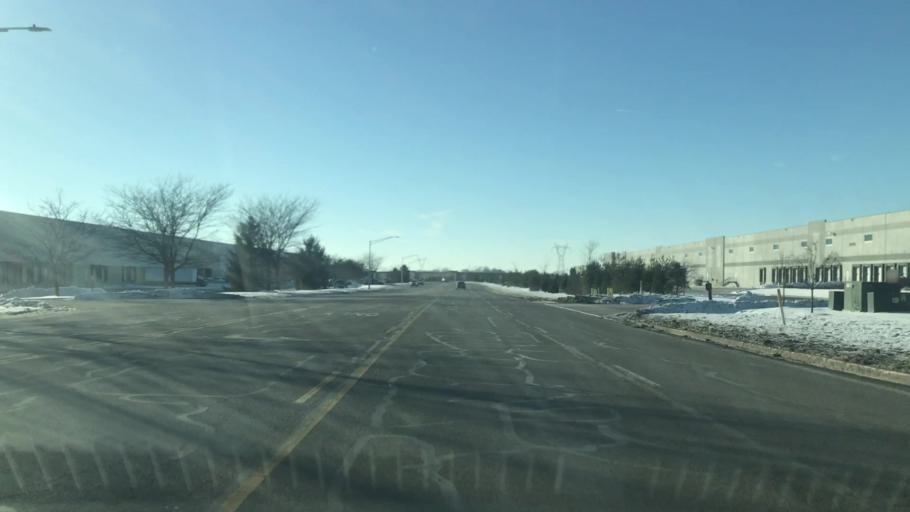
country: US
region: Indiana
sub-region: Hendricks County
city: Plainfield
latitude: 39.6775
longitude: -86.3579
